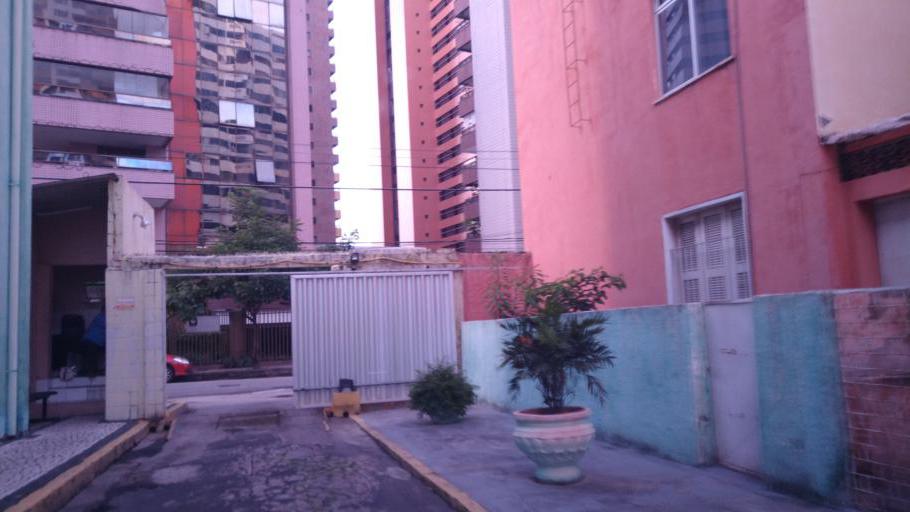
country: BR
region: Ceara
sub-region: Fortaleza
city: Fortaleza
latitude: -3.7250
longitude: -38.4885
